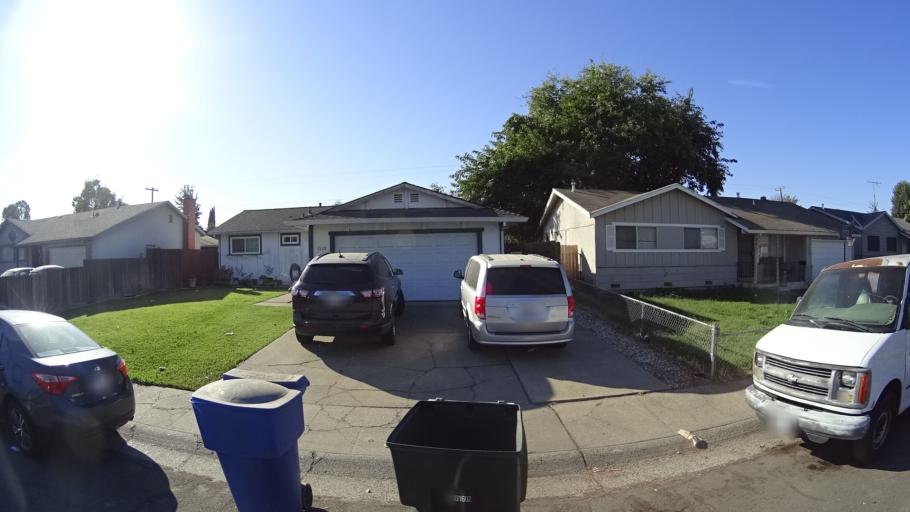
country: US
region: California
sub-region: Sacramento County
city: Parkway
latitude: 38.4781
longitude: -121.4993
